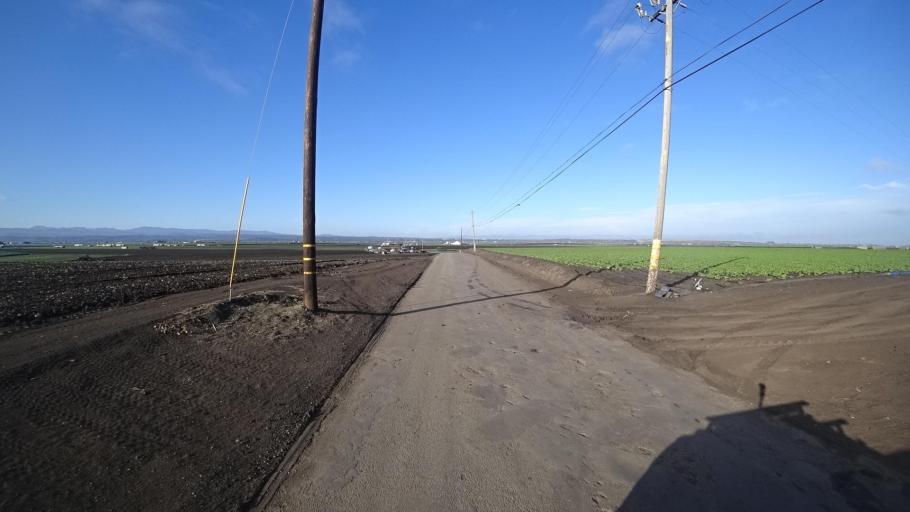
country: US
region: California
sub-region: Monterey County
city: Boronda
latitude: 36.7066
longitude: -121.7019
